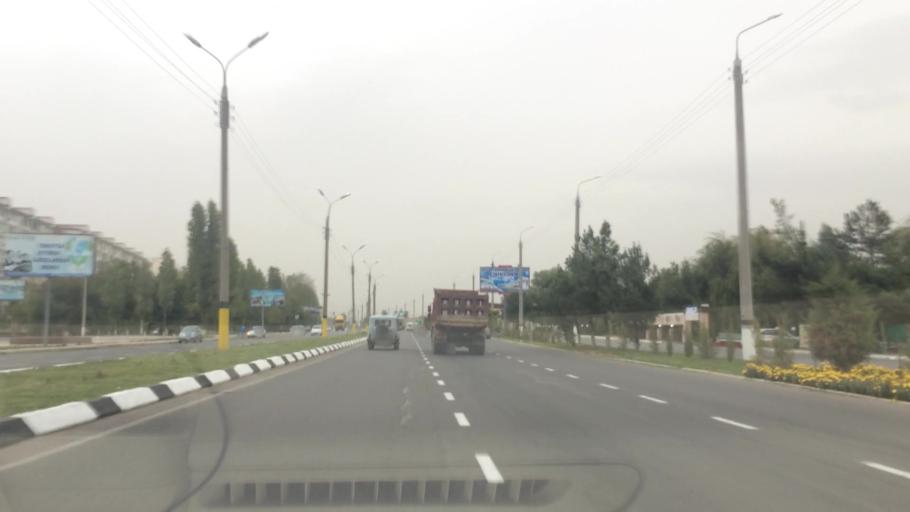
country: UZ
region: Toshkent
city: Salor
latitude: 41.3147
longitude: 69.3528
